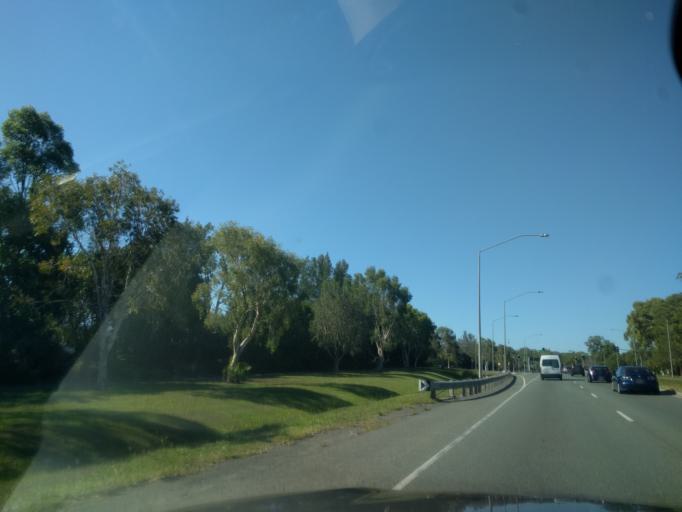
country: AU
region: Queensland
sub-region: Brisbane
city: Sunnybank Hills
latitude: -27.6211
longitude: 153.0496
